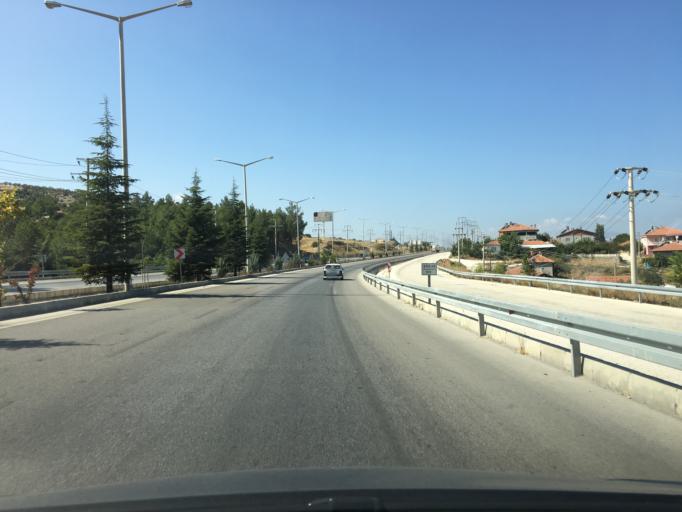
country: TR
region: Burdur
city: Burdur
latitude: 37.7523
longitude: 30.3328
